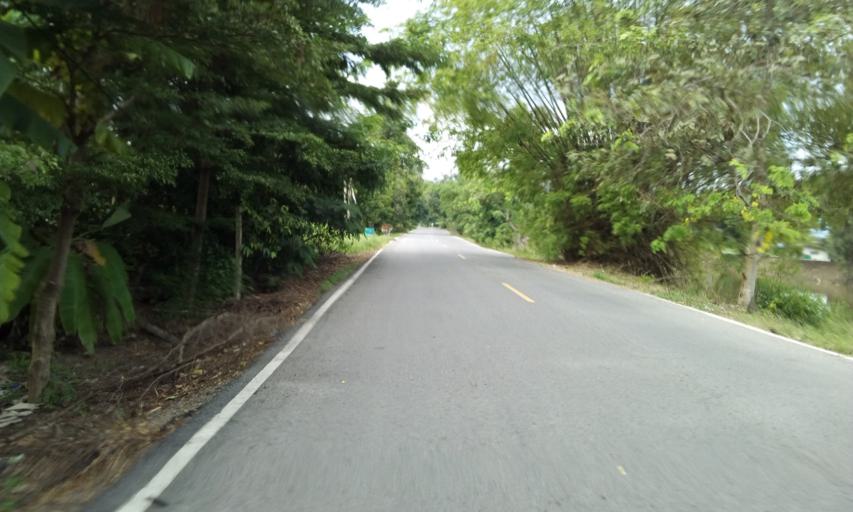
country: TH
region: Pathum Thani
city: Nong Suea
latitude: 14.1857
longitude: 100.8230
